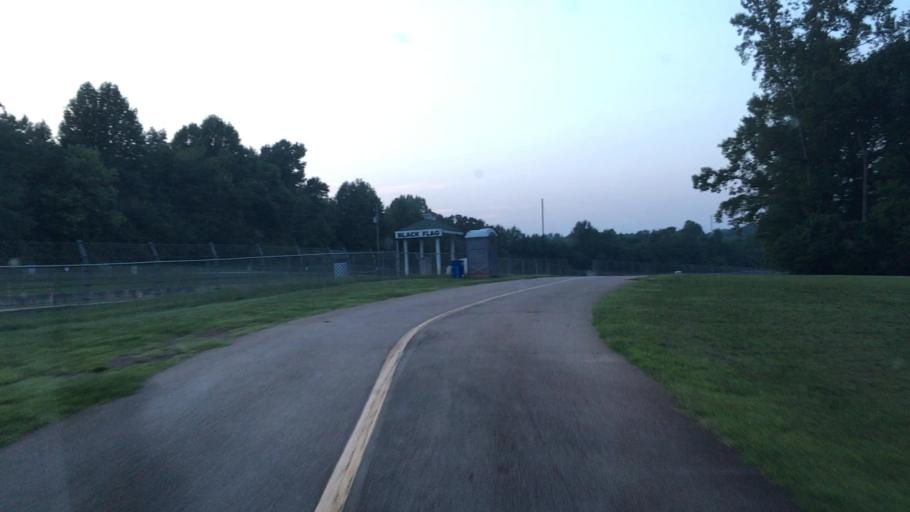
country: US
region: Georgia
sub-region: Jackson County
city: Braselton
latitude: 34.1436
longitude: -83.8184
